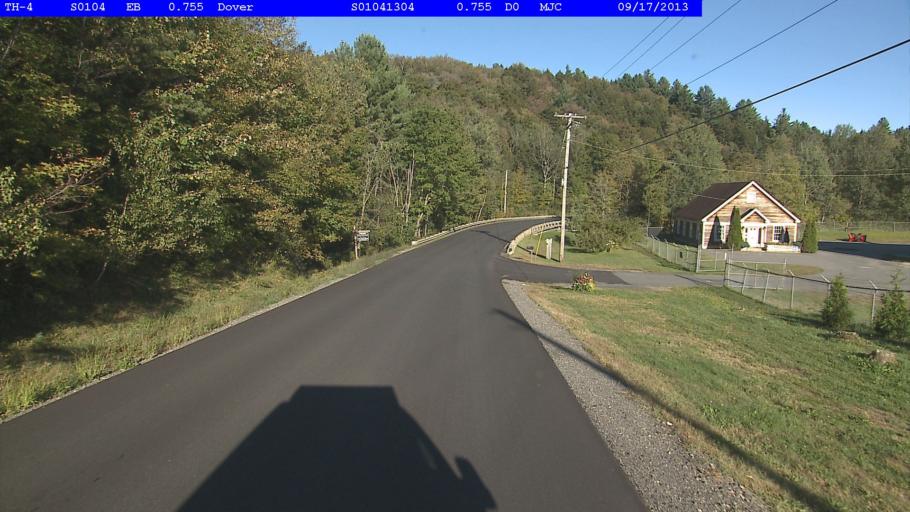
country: US
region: Vermont
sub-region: Windham County
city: Dover
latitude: 42.9289
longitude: -72.8418
